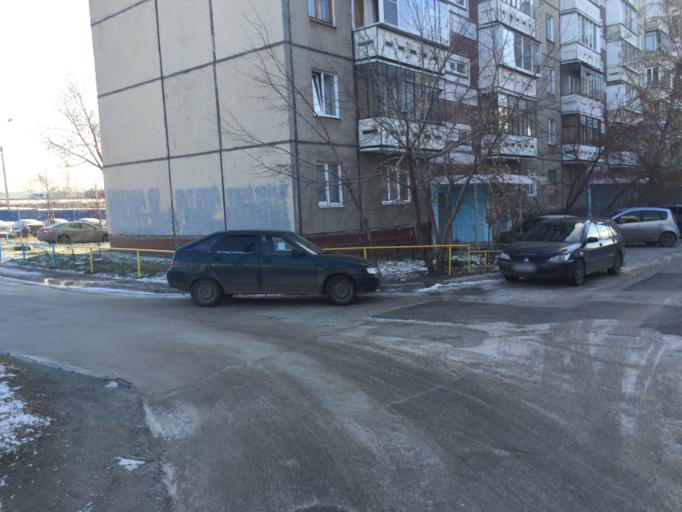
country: RU
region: Chelyabinsk
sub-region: Gorod Chelyabinsk
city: Chelyabinsk
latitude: 55.1695
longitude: 61.4254
